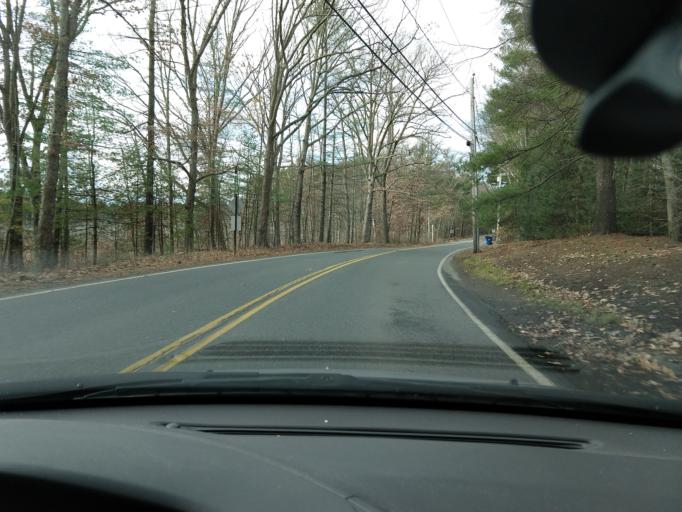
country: US
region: Massachusetts
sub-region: Middlesex County
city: Sudbury
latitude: 42.4063
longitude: -71.3840
